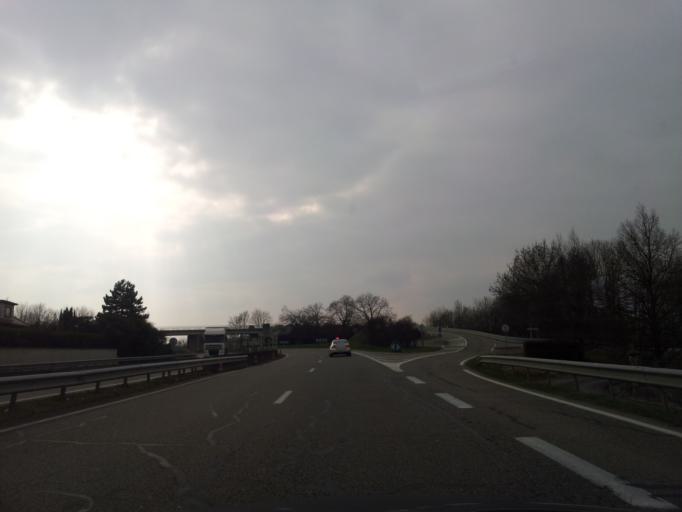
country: FR
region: Alsace
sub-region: Departement du Bas-Rhin
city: Huttenheim
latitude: 48.3476
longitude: 7.5494
